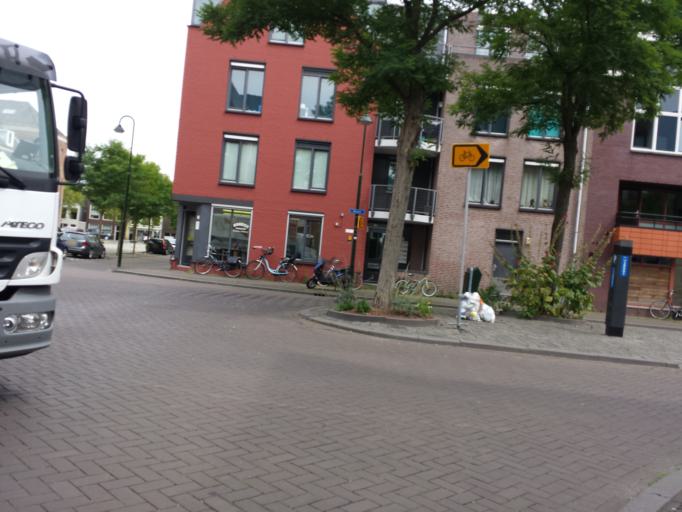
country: NL
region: South Holland
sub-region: Gemeente Gouda
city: Gouda
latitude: 52.0104
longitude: 4.7045
